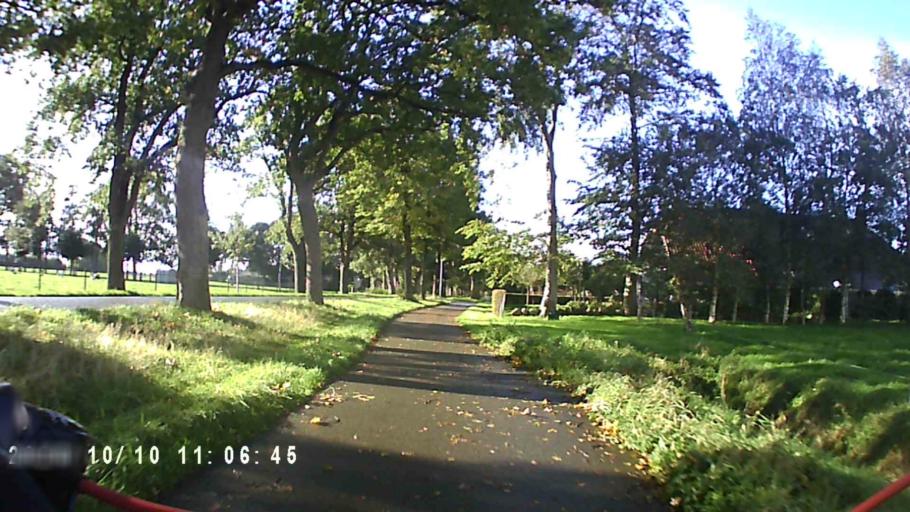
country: NL
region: Friesland
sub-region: Gemeente Achtkarspelen
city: Surhuisterveen
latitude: 53.1252
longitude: 6.2165
